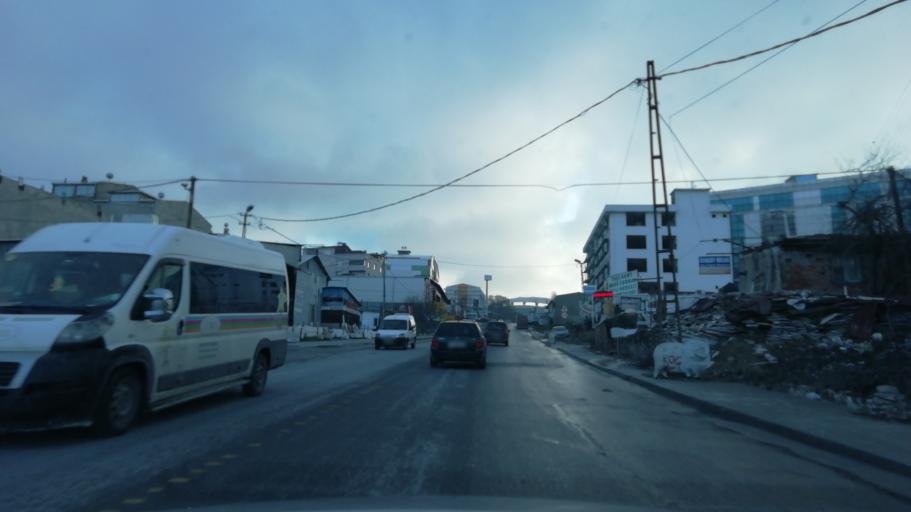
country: TR
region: Istanbul
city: Esenyurt
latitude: 41.0190
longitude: 28.7010
